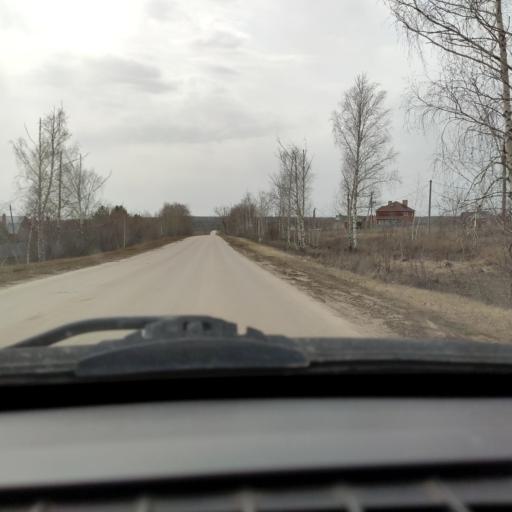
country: RU
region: Samara
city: Dubovyy Umet
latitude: 53.0448
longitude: 50.1824
